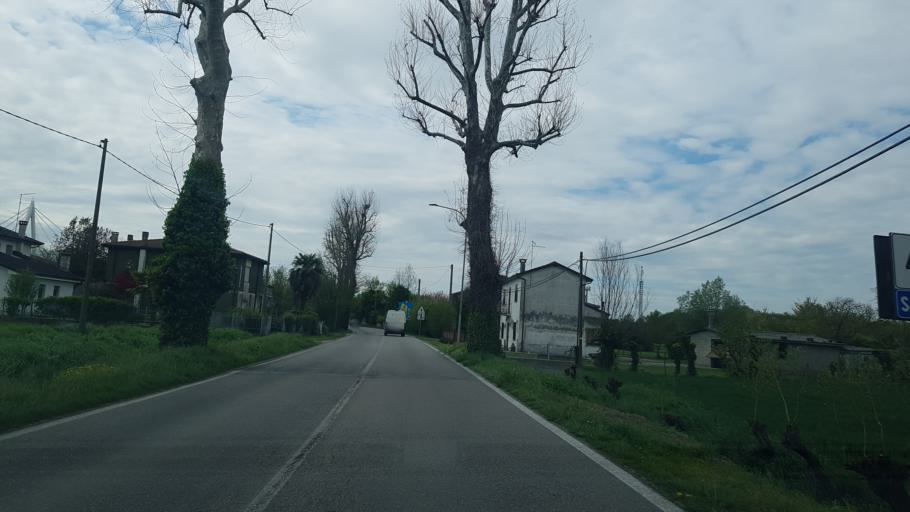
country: IT
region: Veneto
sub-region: Provincia di Padova
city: Piacenza d'Adige
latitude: 45.1267
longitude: 11.5387
